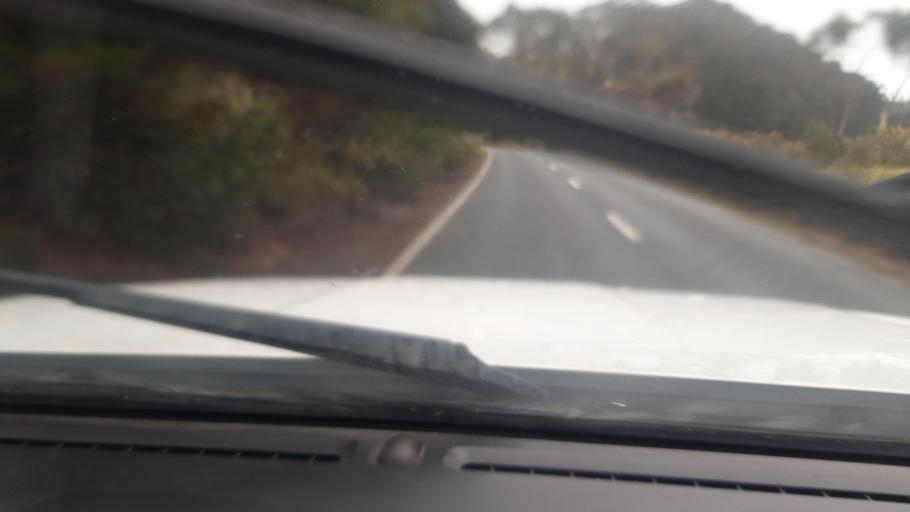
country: NZ
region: Northland
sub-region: Far North District
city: Kaitaia
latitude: -34.9995
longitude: 173.2161
